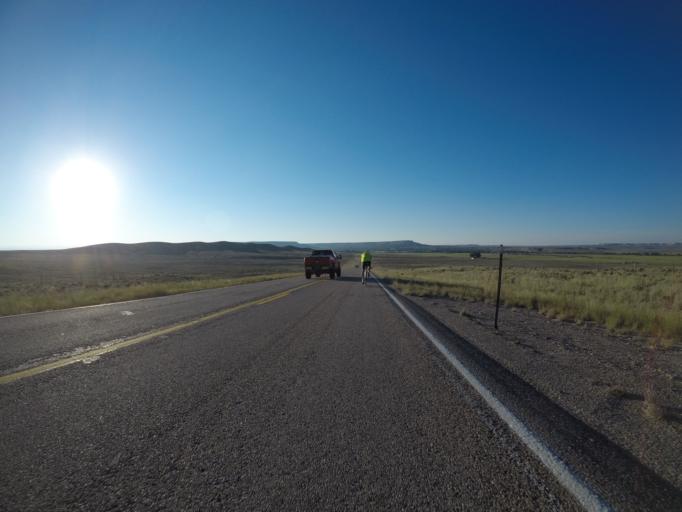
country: US
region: Wyoming
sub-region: Sublette County
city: Marbleton
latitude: 42.5795
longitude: -109.9903
